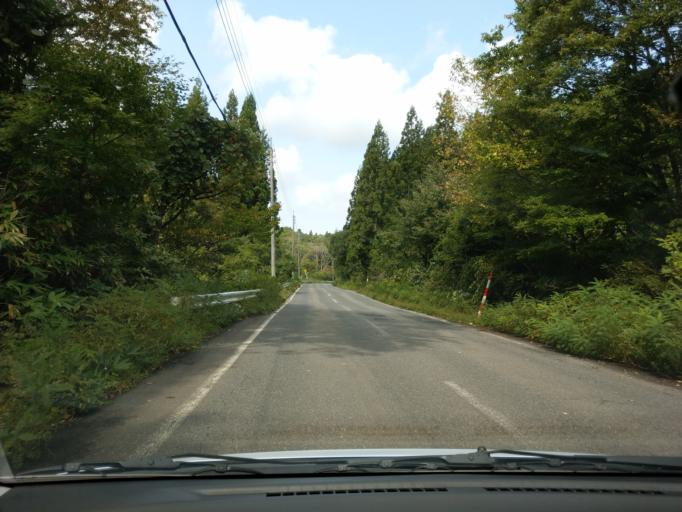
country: JP
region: Akita
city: Omagari
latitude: 39.4609
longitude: 140.3180
